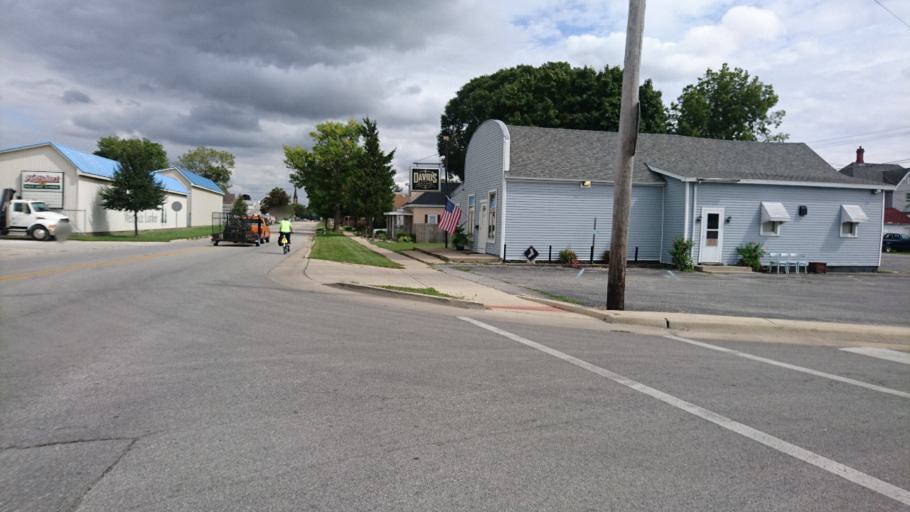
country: US
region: Illinois
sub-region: Livingston County
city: Pontiac
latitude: 40.8810
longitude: -88.6359
